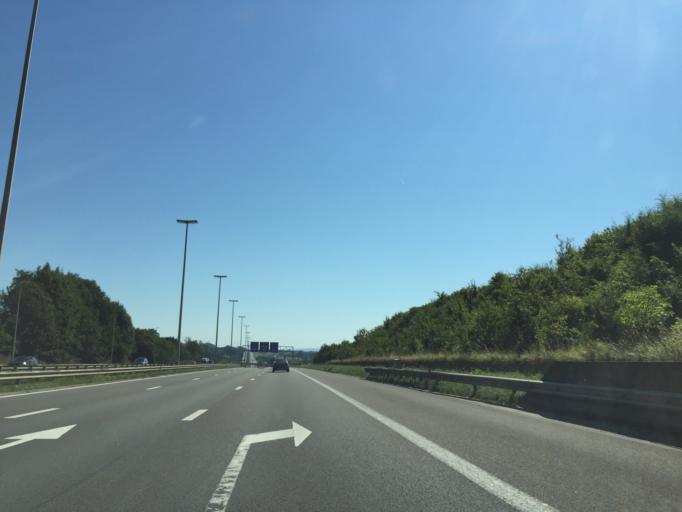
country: BE
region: Wallonia
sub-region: Province de Liege
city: Herve
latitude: 50.6351
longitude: 5.8207
